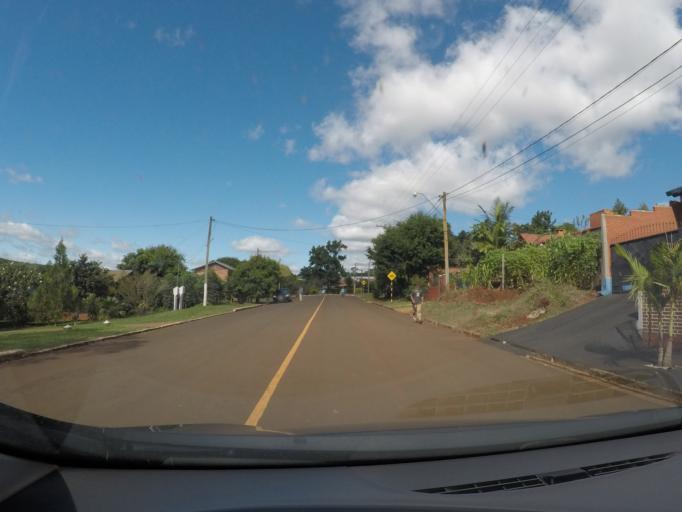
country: AR
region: Misiones
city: Puerto Rico
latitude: -26.8011
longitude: -55.0135
